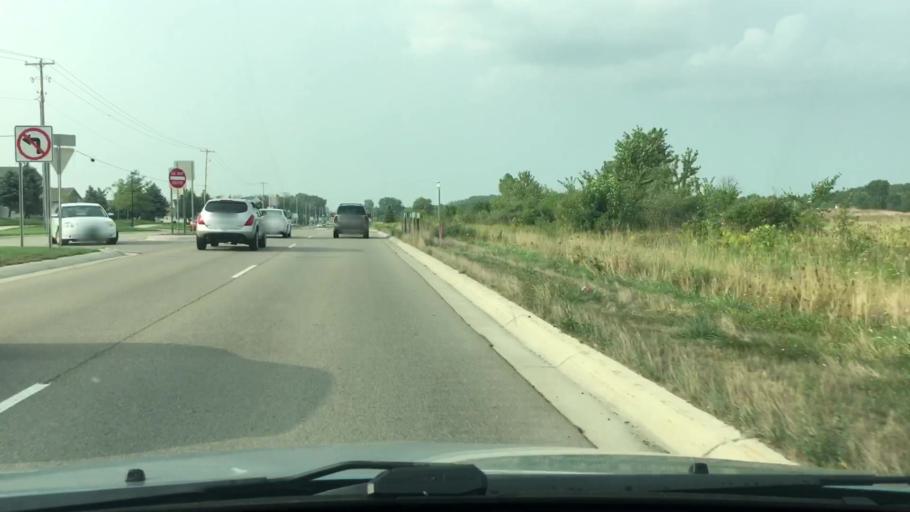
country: US
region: Michigan
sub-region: Ottawa County
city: Allendale
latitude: 42.9587
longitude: -85.9038
